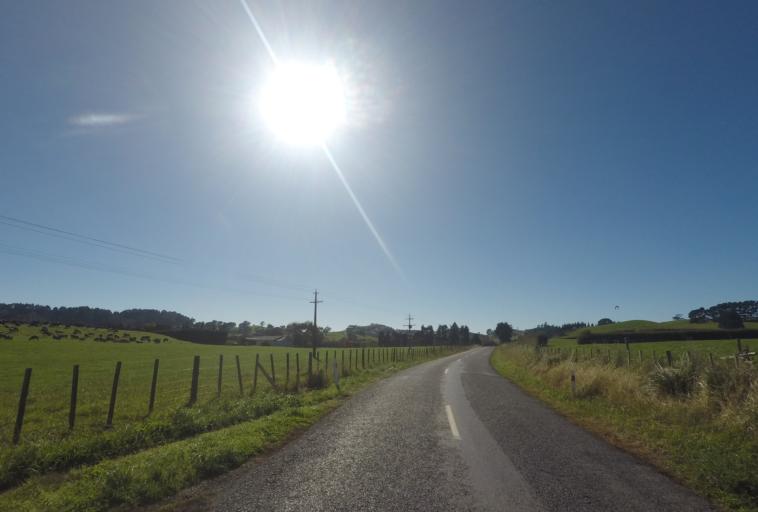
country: NZ
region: Bay of Plenty
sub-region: Western Bay of Plenty District
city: Waihi Beach
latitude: -37.4124
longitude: 175.8910
